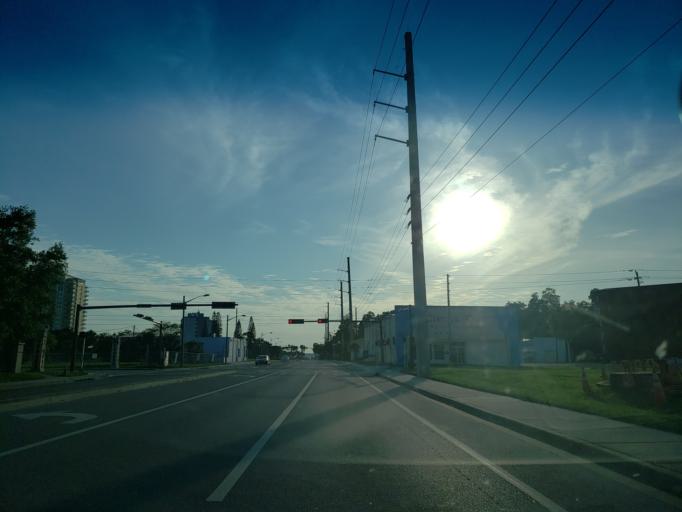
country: US
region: Florida
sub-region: Sarasota County
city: Sarasota
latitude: 27.3449
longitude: -82.5421
